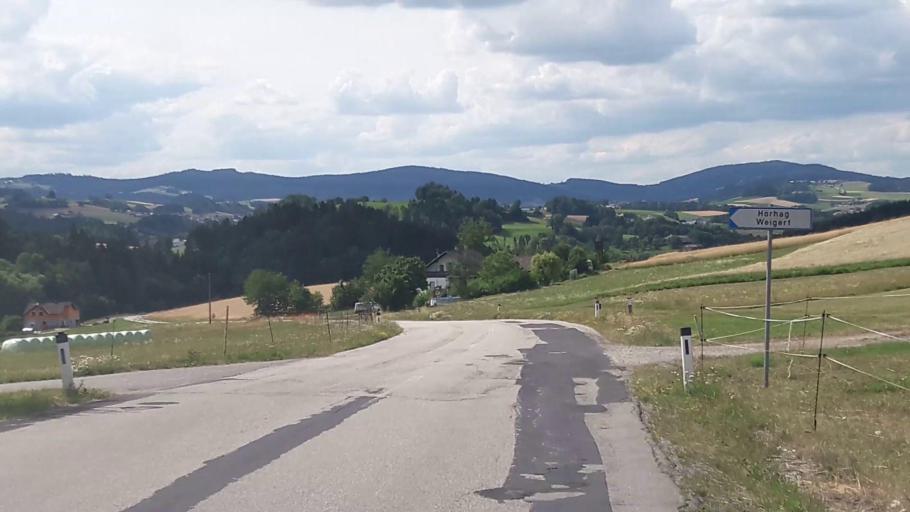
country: AT
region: Upper Austria
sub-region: Politischer Bezirk Rohrbach
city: Atzesberg
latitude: 48.4740
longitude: 13.9484
